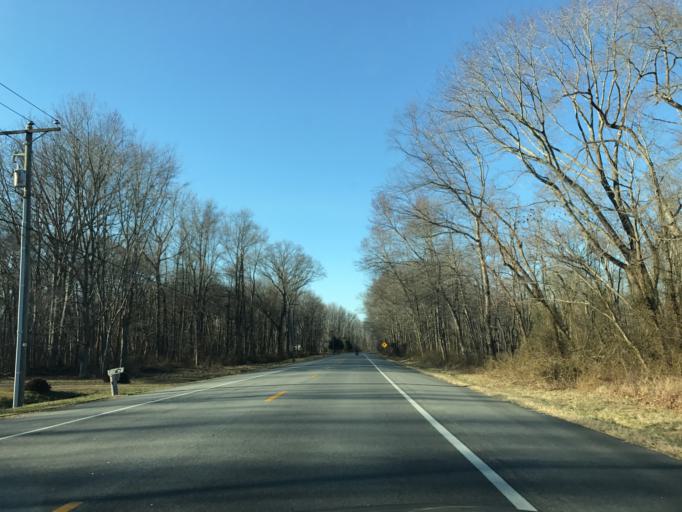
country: US
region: Maryland
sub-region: Queen Anne's County
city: Kingstown
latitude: 39.2298
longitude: -75.8718
